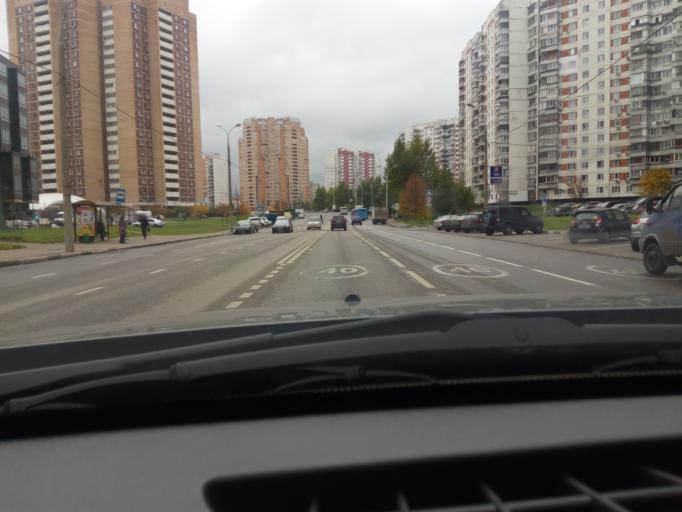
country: RU
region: Moskovskaya
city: Reutov
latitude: 55.7399
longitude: 37.8591
